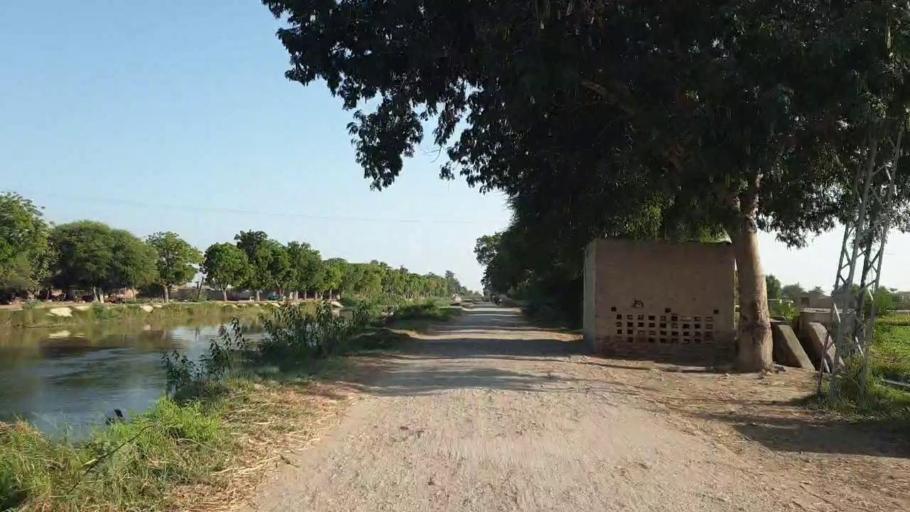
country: PK
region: Sindh
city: Hyderabad
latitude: 25.3205
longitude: 68.4278
